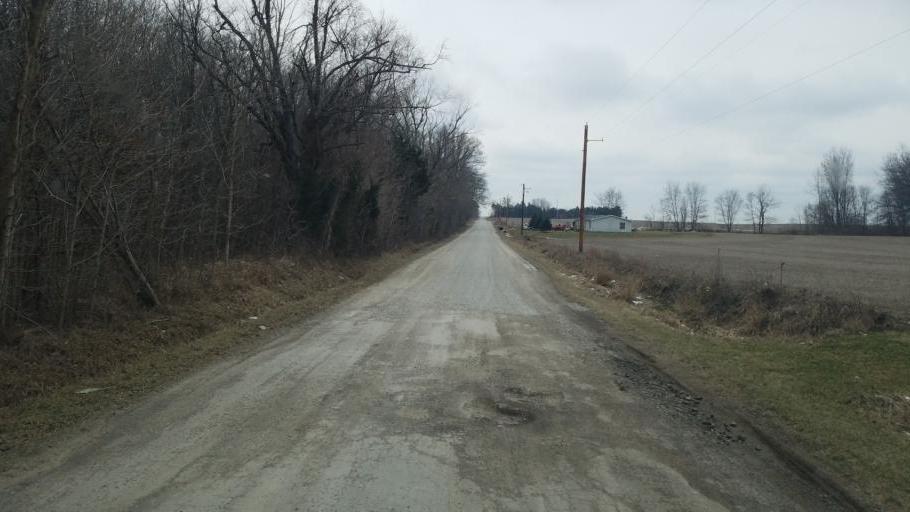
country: US
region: Ohio
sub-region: Morrow County
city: Mount Gilead
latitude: 40.5311
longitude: -82.7110
